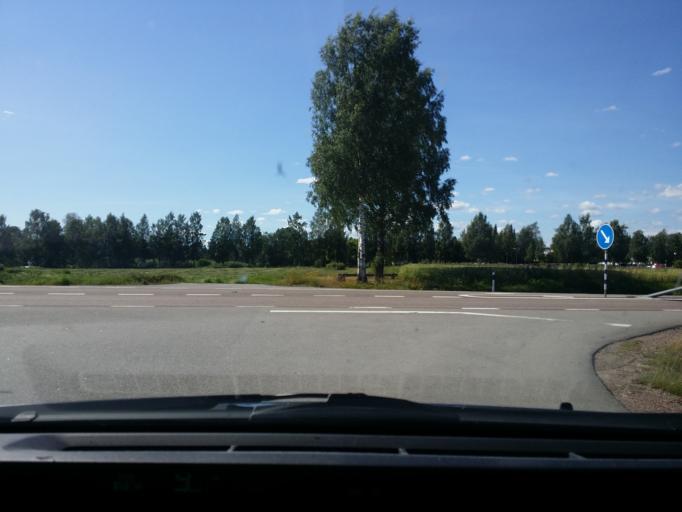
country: SE
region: Dalarna
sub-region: Hedemora Kommun
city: Brunna
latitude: 60.2727
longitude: 16.0021
